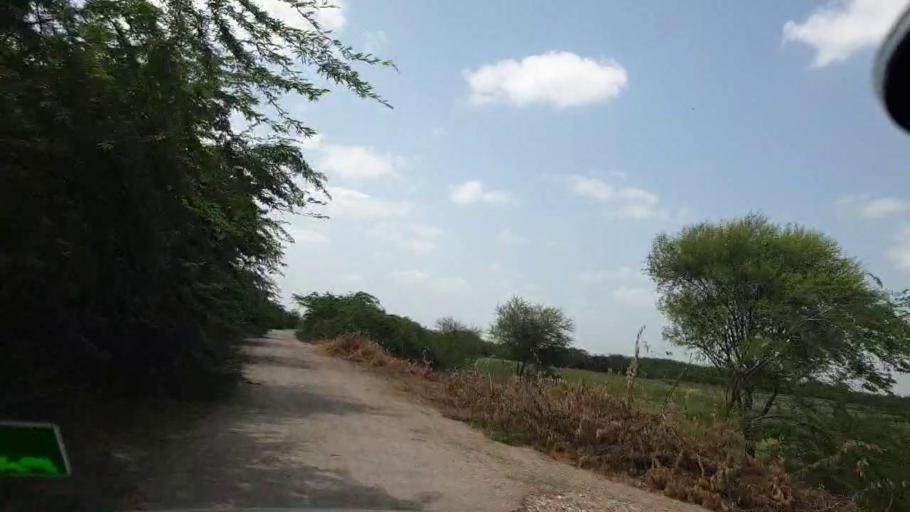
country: PK
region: Sindh
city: Kadhan
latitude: 24.5518
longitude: 69.1943
